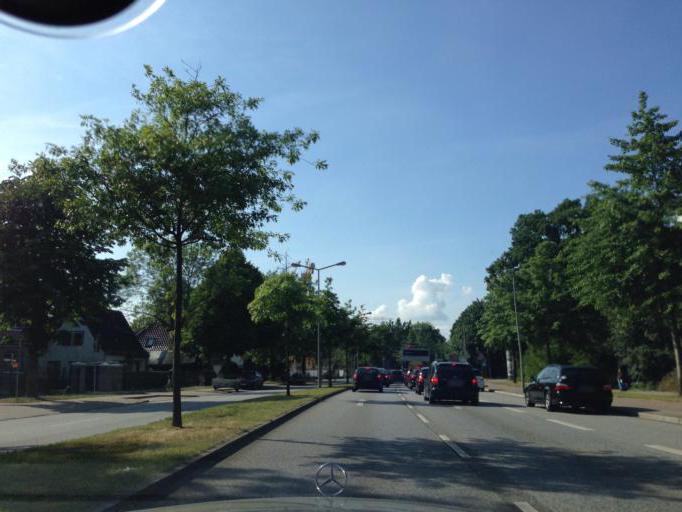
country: DE
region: Hamburg
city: Alsterdorf
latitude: 53.6162
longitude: 10.0167
